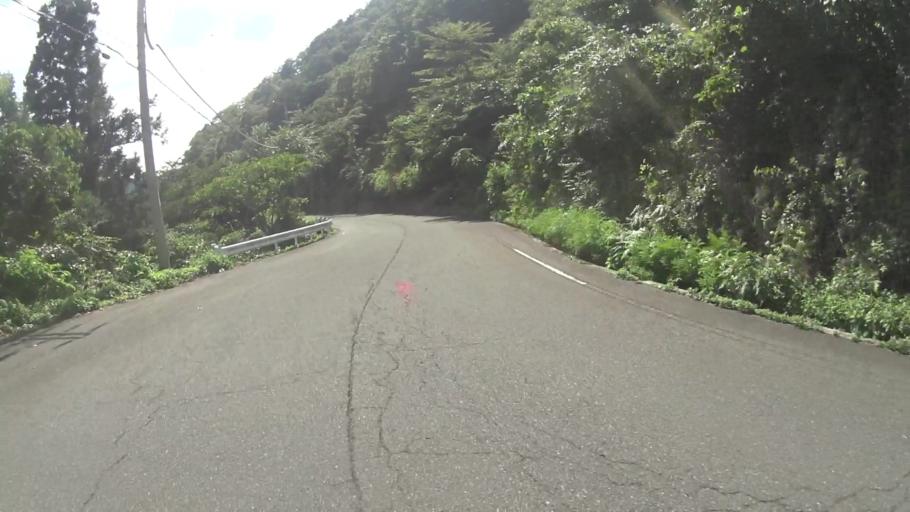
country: JP
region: Kyoto
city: Miyazu
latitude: 35.7120
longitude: 135.1941
